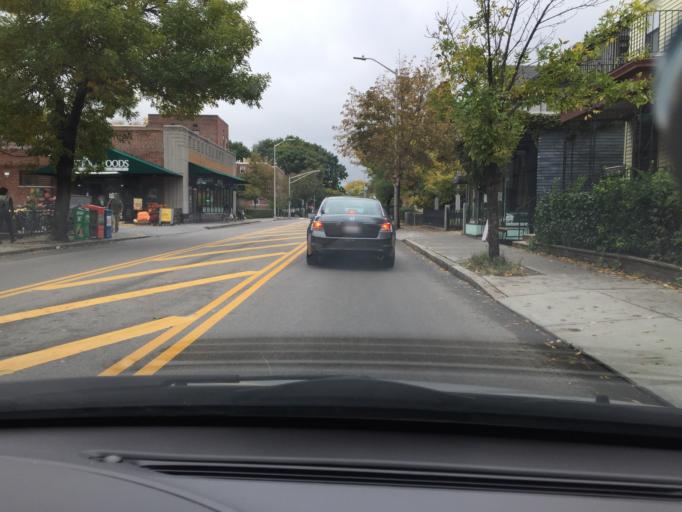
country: US
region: Massachusetts
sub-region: Middlesex County
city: Cambridge
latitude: 42.3675
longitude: -71.1022
